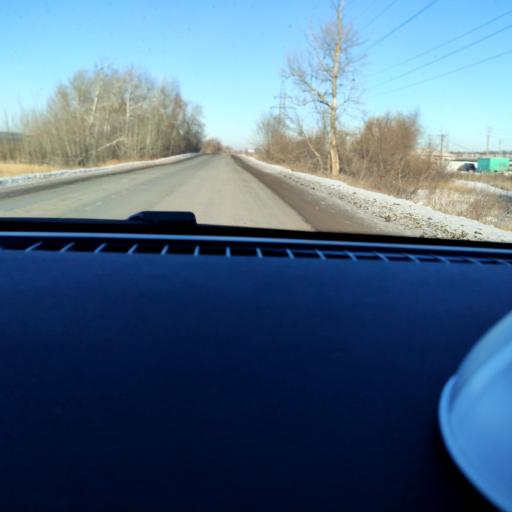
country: RU
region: Samara
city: Spiridonovka
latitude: 53.1077
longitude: 50.6409
